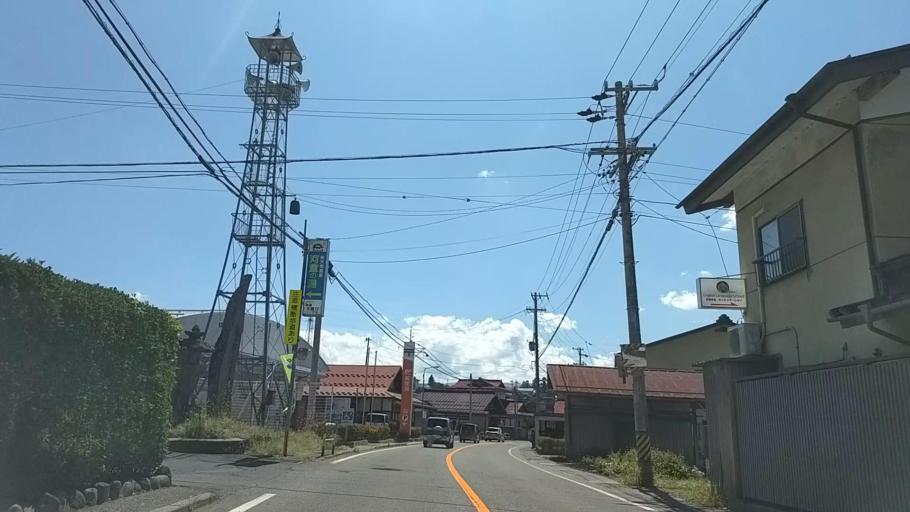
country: JP
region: Nagano
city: Chino
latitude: 36.0396
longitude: 138.2251
